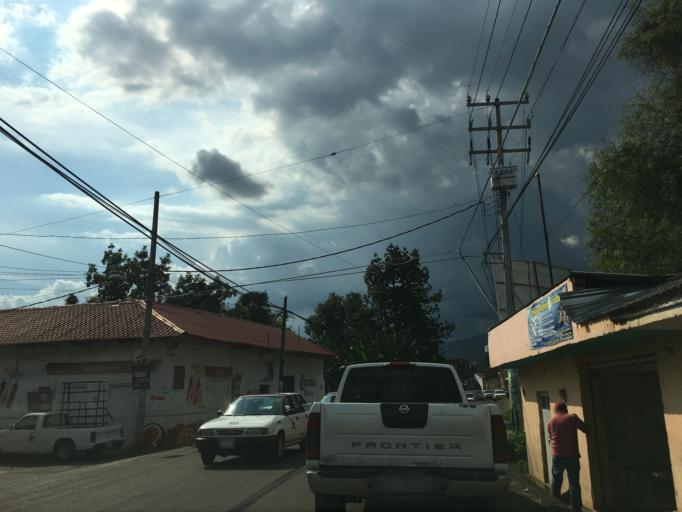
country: MX
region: Michoacan
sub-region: Ziracuaretiro
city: Patuan
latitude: 19.4179
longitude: -101.9102
